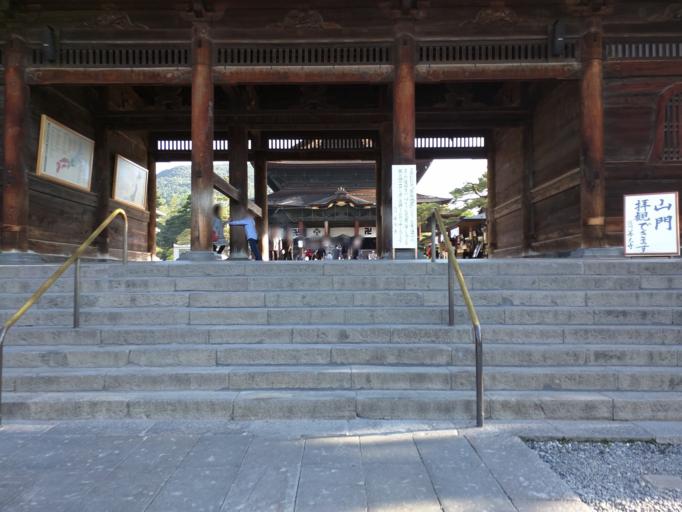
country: JP
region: Nagano
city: Nagano-shi
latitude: 36.6606
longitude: 138.1876
